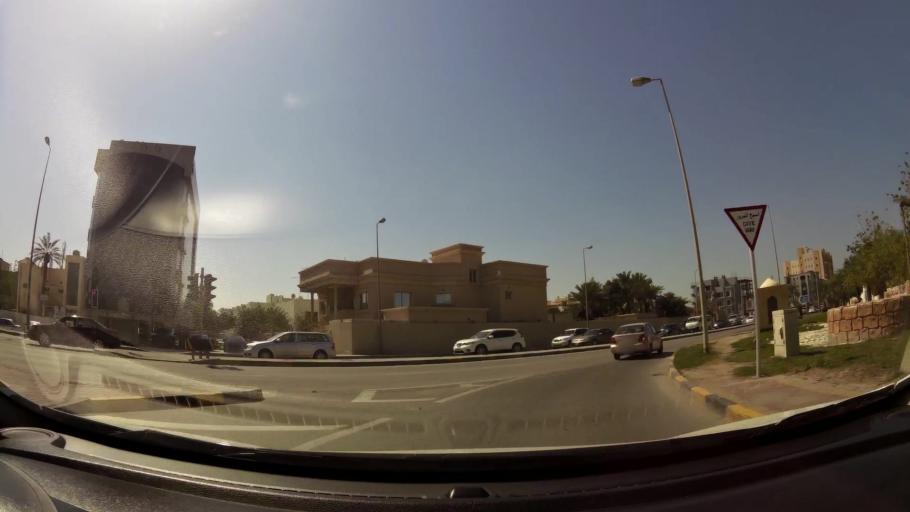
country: BH
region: Manama
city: Manama
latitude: 26.2129
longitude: 50.5828
